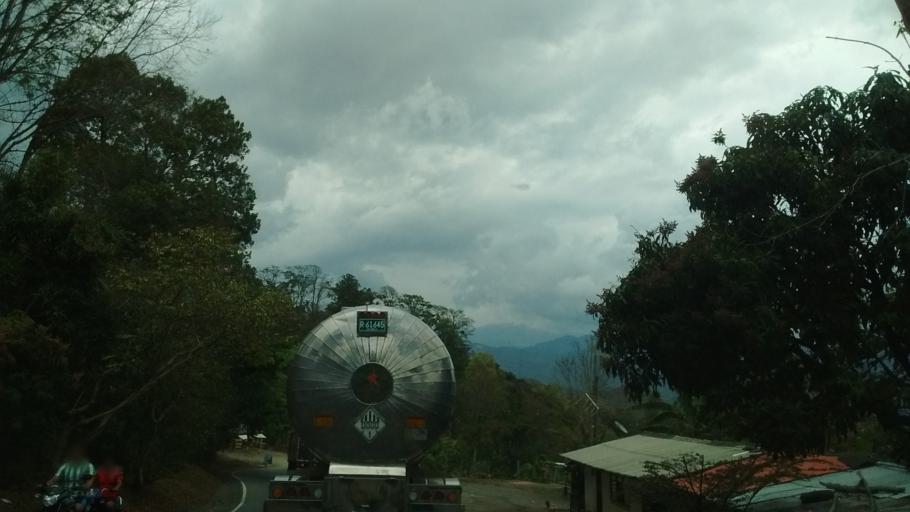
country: CO
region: Cauca
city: Rosas
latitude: 2.2950
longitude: -76.7060
